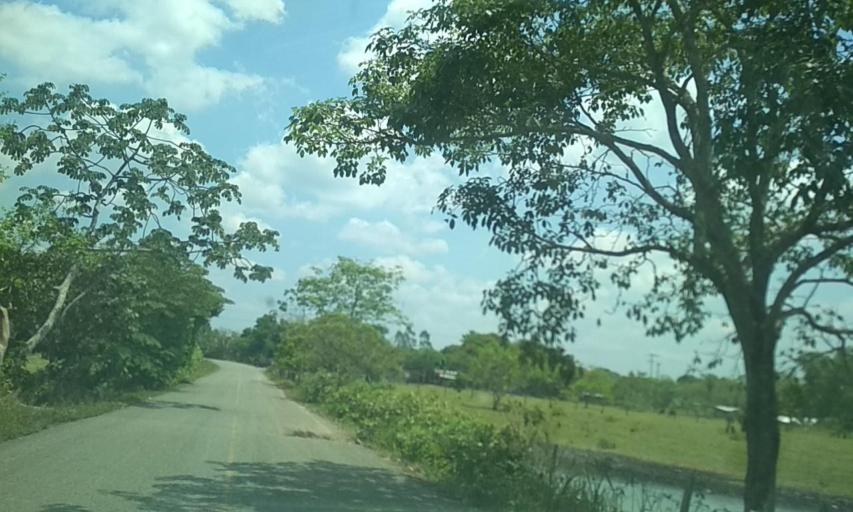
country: MX
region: Tabasco
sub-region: Huimanguillo
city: Francisco Rueda
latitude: 17.7928
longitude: -93.8511
